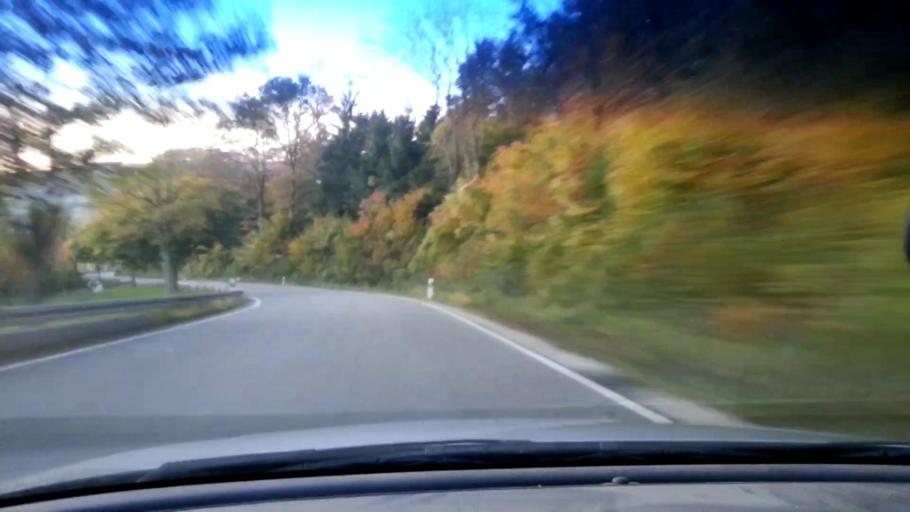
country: DE
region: Bavaria
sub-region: Upper Franconia
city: Litzendorf
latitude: 49.8703
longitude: 11.0748
